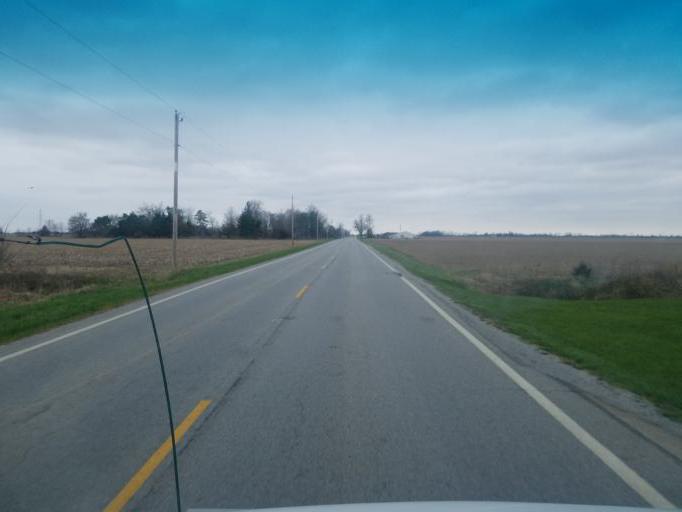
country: US
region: Ohio
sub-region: Allen County
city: Delphos
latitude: 40.9323
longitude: -84.4128
